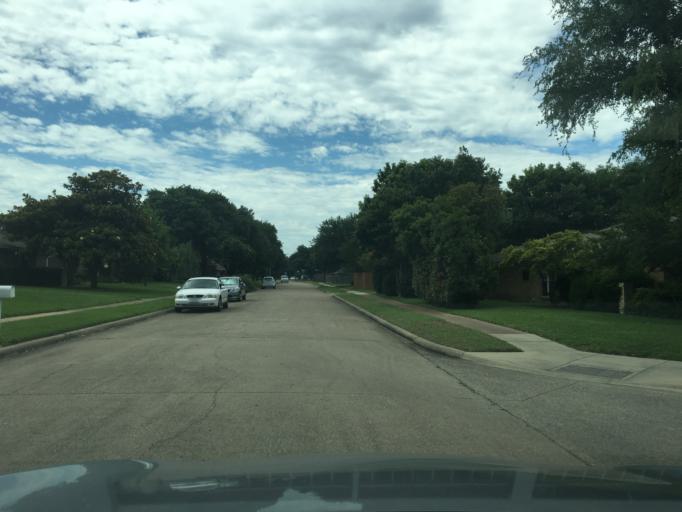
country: US
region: Texas
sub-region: Dallas County
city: Richardson
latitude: 32.9406
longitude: -96.7007
